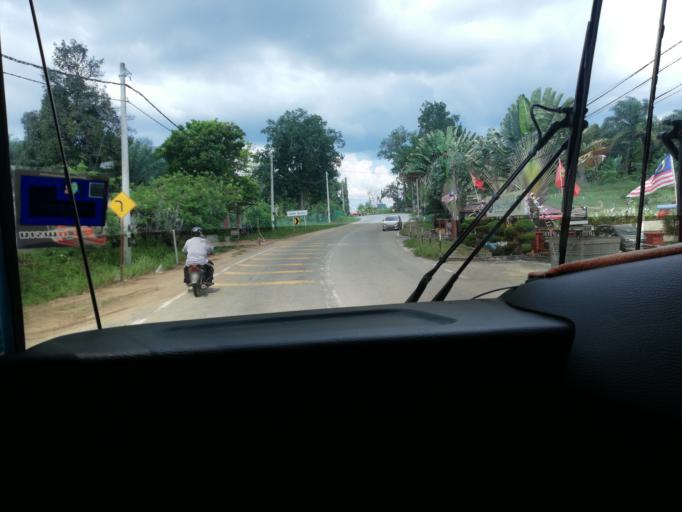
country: MY
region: Perak
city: Parit Buntar
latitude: 5.1373
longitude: 100.5867
